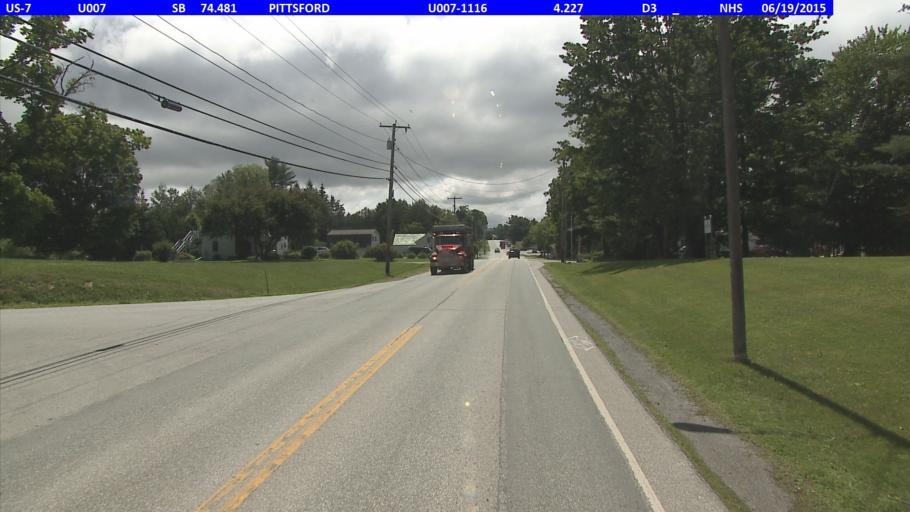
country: US
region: Vermont
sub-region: Rutland County
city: Brandon
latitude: 43.7103
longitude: -73.0324
